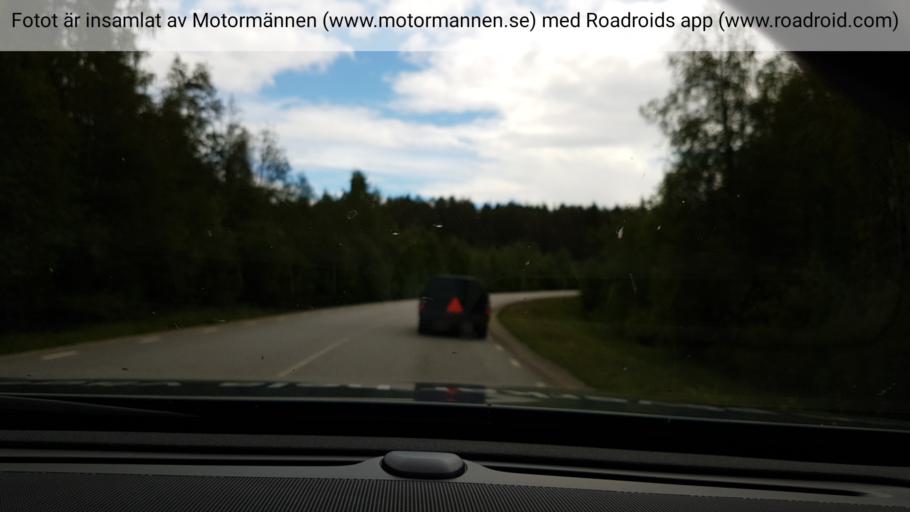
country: SE
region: Vaesterbotten
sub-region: Vindelns Kommun
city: Vindeln
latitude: 64.2058
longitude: 19.6828
